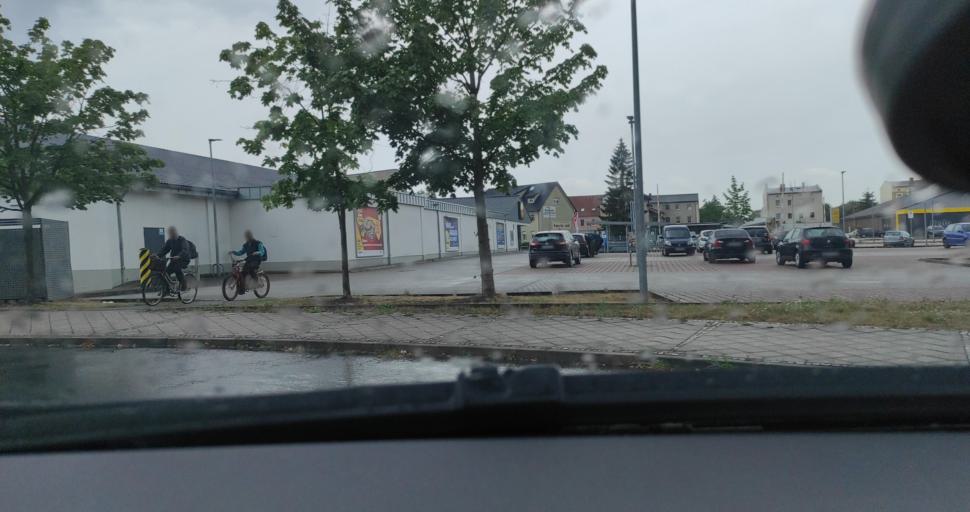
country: DE
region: Brandenburg
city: Forst
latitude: 51.7367
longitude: 14.6397
